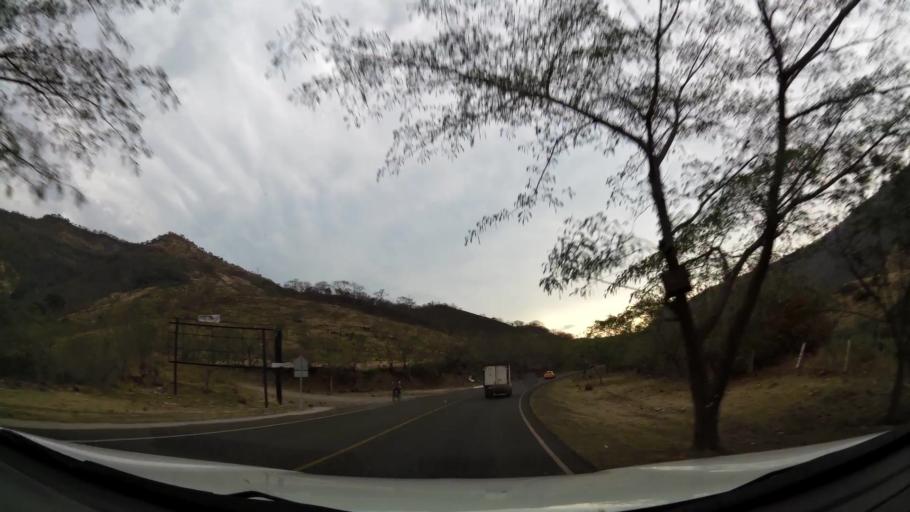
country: NI
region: Leon
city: Santa Rosa del Penon
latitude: 12.9377
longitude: -86.2175
